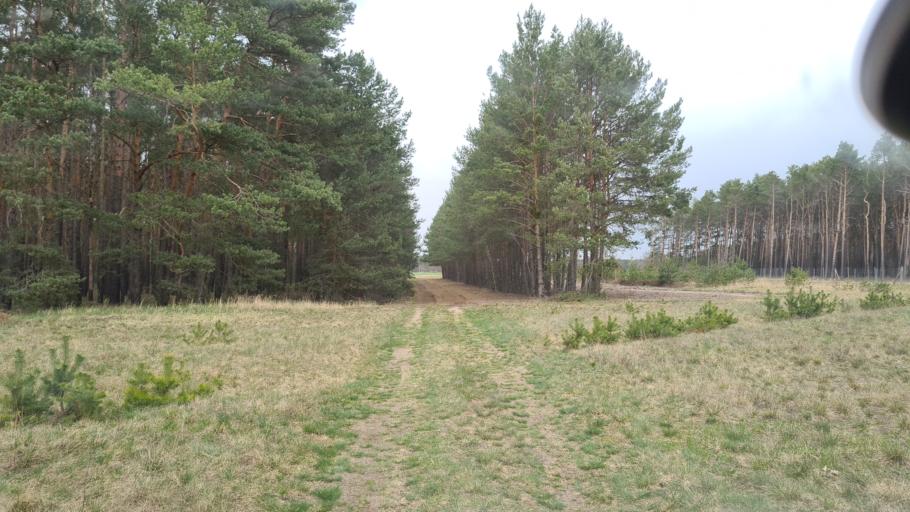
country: DE
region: Brandenburg
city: Finsterwalde
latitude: 51.5683
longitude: 13.6815
